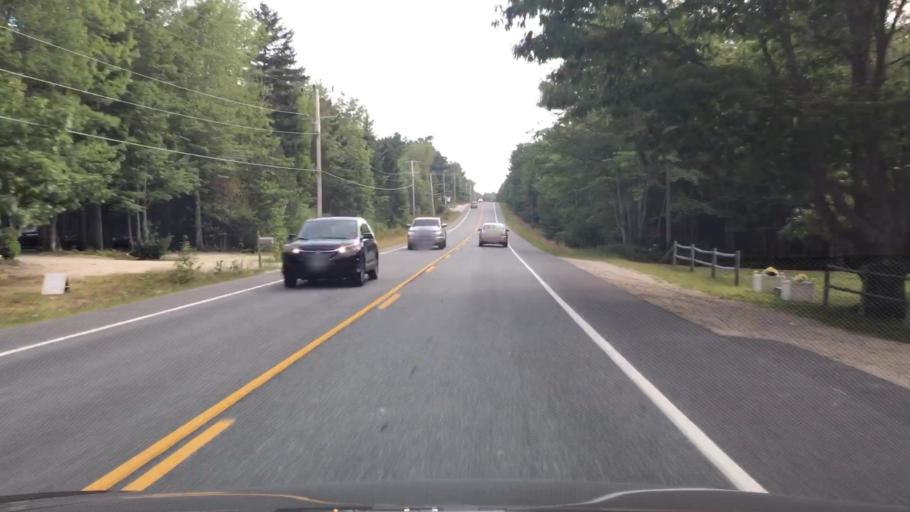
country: US
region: Maine
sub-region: Hancock County
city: Surry
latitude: 44.4494
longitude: -68.5585
